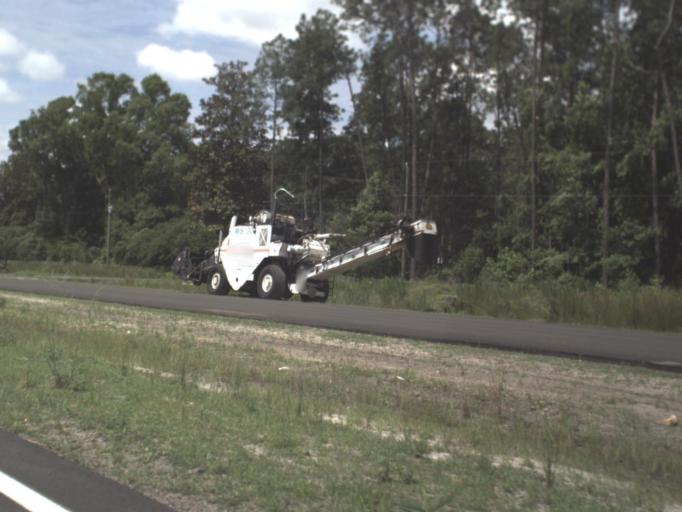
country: US
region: Florida
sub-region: Nassau County
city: Nassau Village-Ratliff
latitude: 30.4678
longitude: -81.9091
